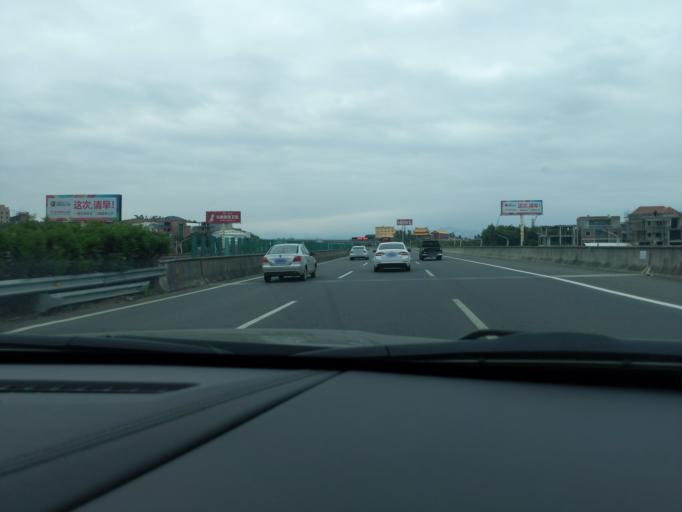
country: CN
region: Fujian
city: Cizao
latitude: 24.7817
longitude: 118.5040
